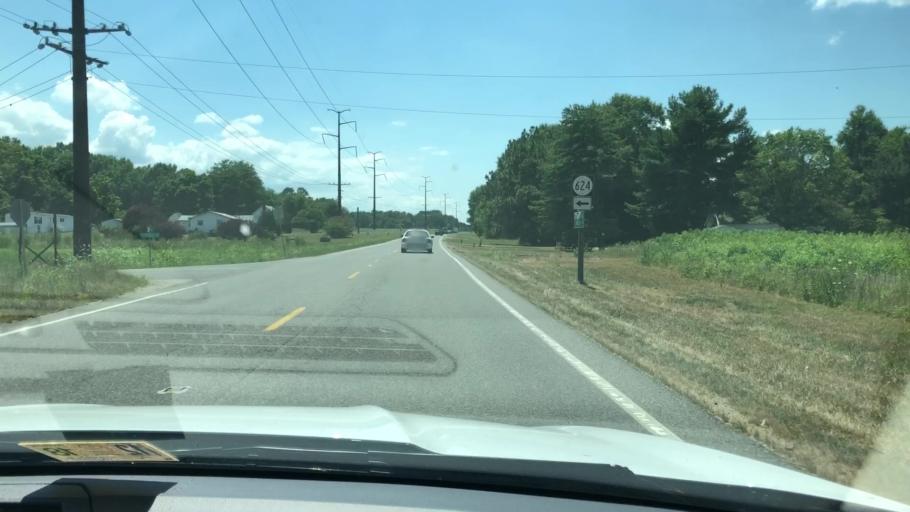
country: US
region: Virginia
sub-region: Middlesex County
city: Saluda
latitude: 37.5883
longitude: -76.4741
